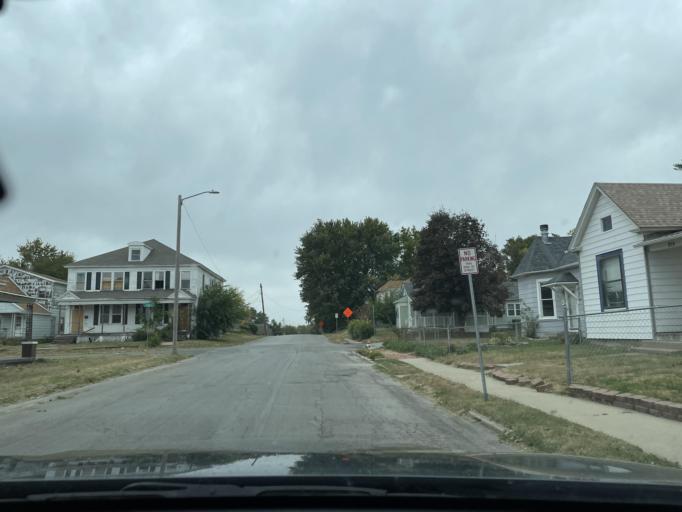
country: US
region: Missouri
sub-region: Buchanan County
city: Saint Joseph
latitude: 39.7748
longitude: -94.8442
